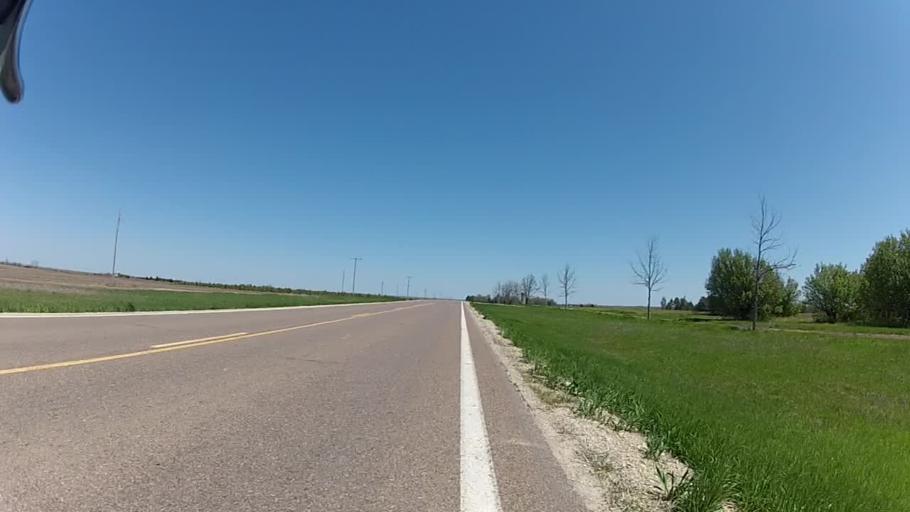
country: US
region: Kansas
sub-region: Riley County
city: Manhattan
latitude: 38.9611
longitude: -96.5200
